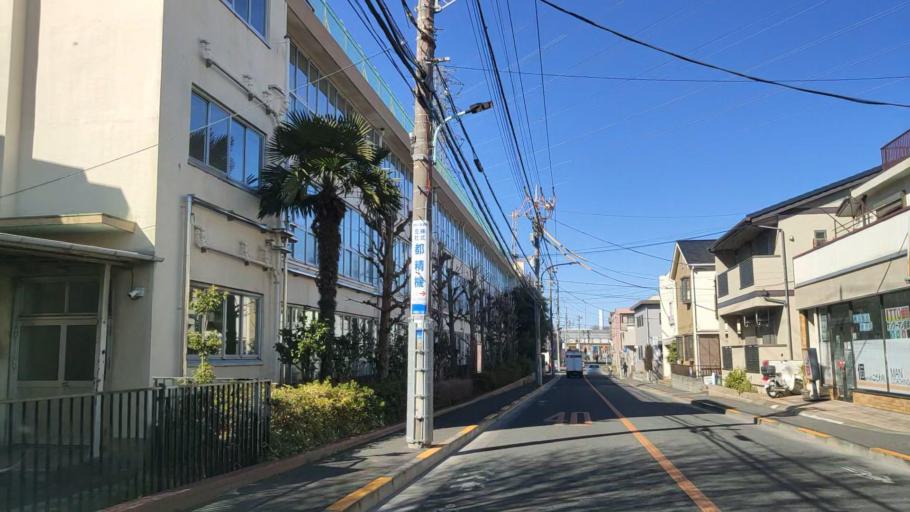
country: JP
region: Tokyo
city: Mitaka-shi
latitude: 35.6698
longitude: 139.5722
